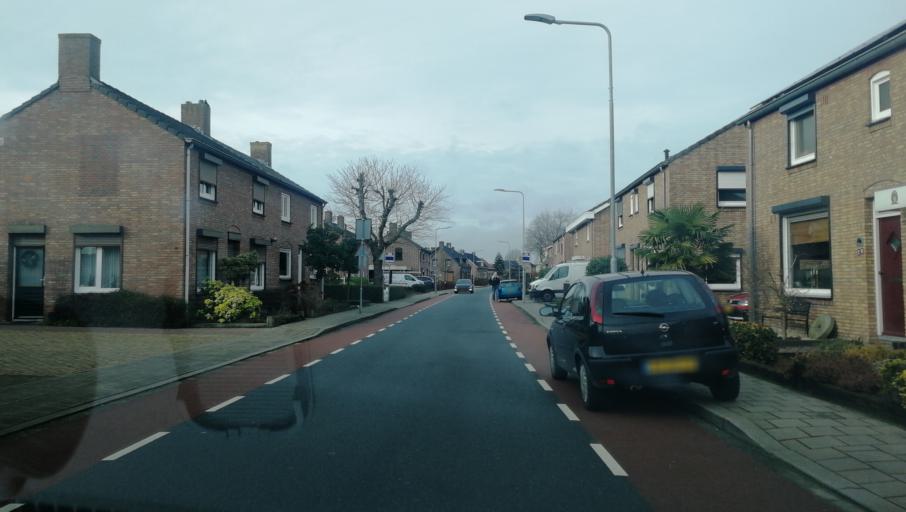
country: NL
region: Limburg
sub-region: Gemeente Beesel
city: Offenbeek
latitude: 51.3091
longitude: 6.1160
